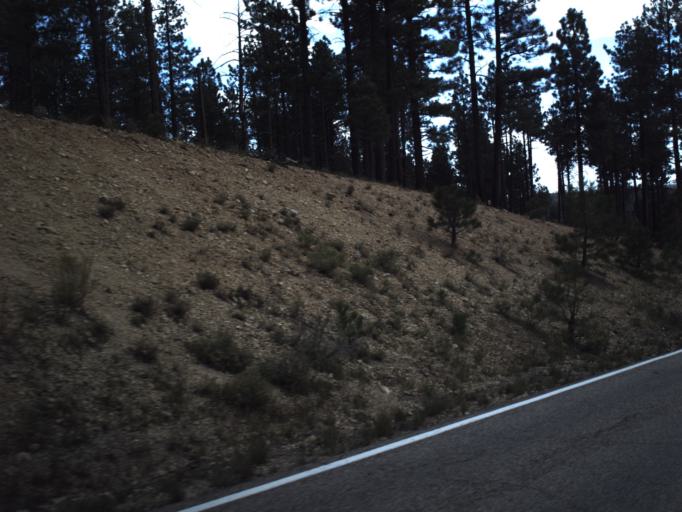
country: US
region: Utah
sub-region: Garfield County
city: Panguitch
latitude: 37.4952
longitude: -112.6205
